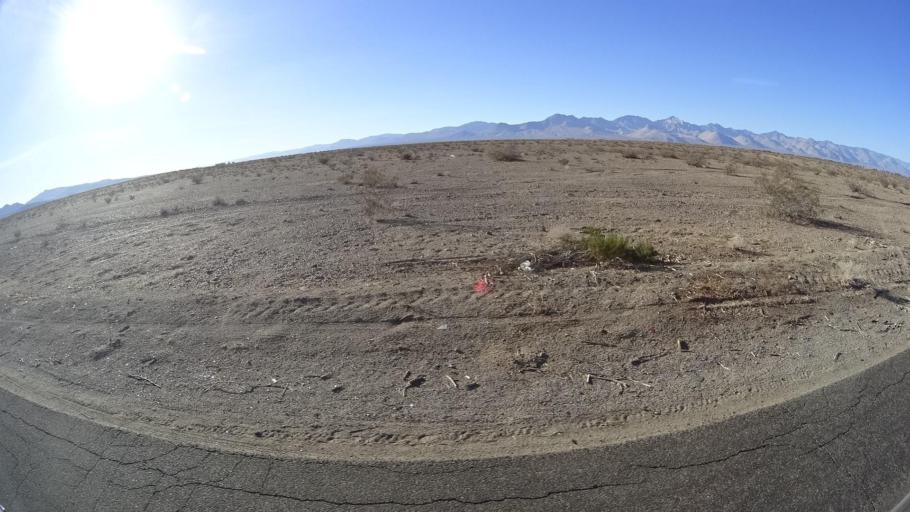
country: US
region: California
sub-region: Kern County
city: China Lake Acres
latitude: 35.6139
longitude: -117.7231
